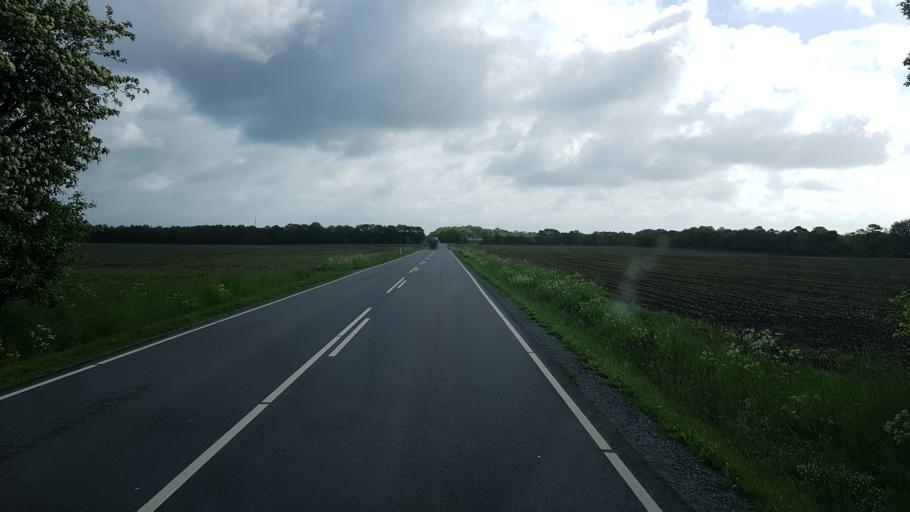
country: DK
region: South Denmark
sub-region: Vejen Kommune
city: Vejen
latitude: 55.4559
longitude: 9.1590
